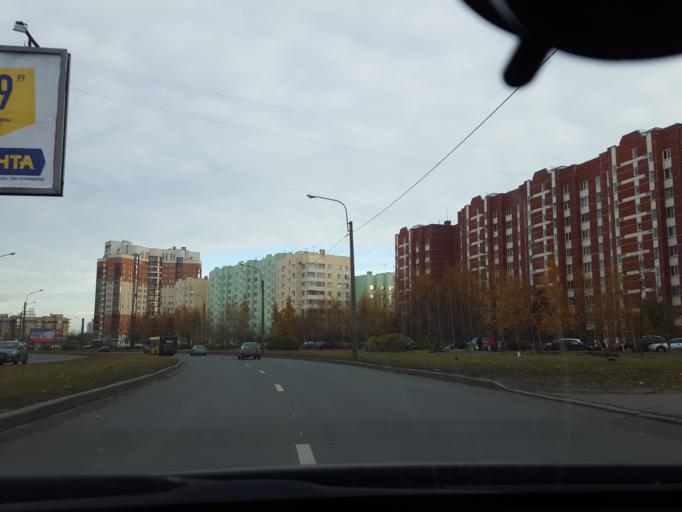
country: RU
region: St.-Petersburg
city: Kolomyagi
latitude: 60.0228
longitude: 30.2843
